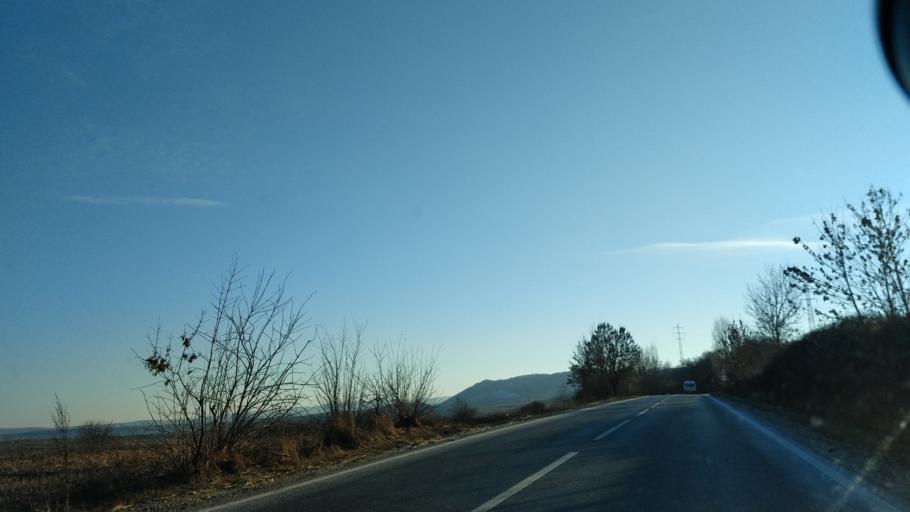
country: RO
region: Bacau
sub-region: Comuna Helegiu
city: Bratila
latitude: 46.2985
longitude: 26.7523
